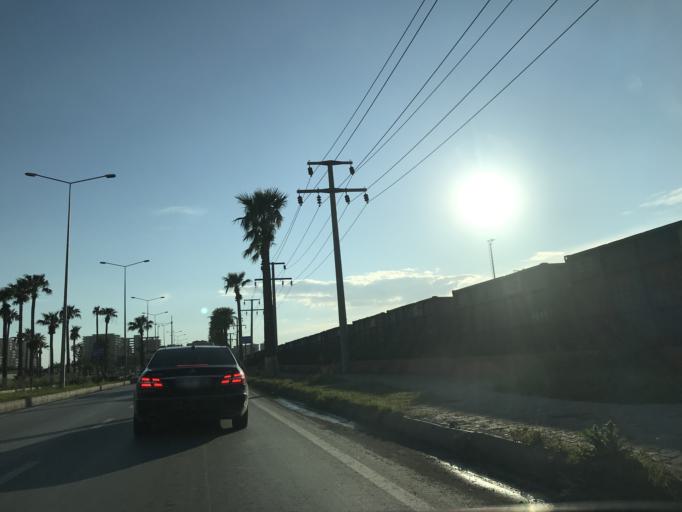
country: TR
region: Hatay
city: Iskenderun
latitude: 36.5901
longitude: 36.1899
